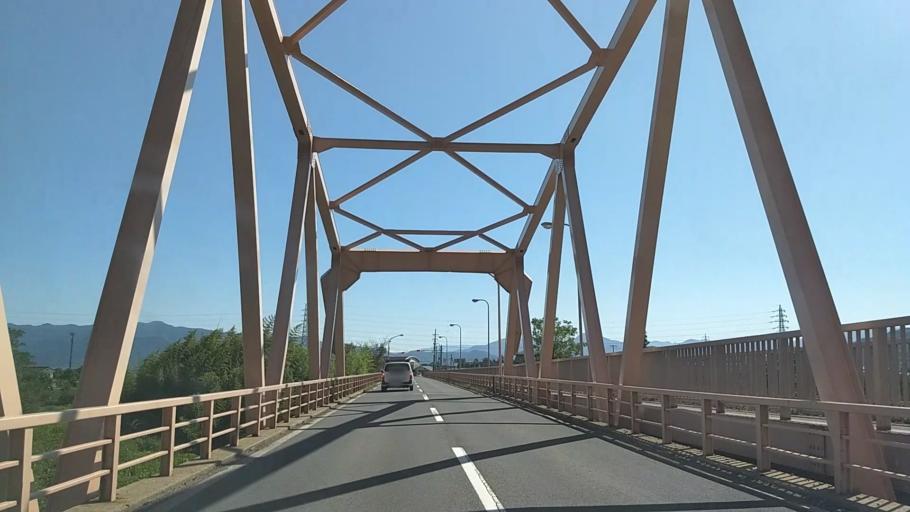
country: JP
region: Nagano
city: Nagano-shi
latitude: 36.6209
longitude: 138.1415
